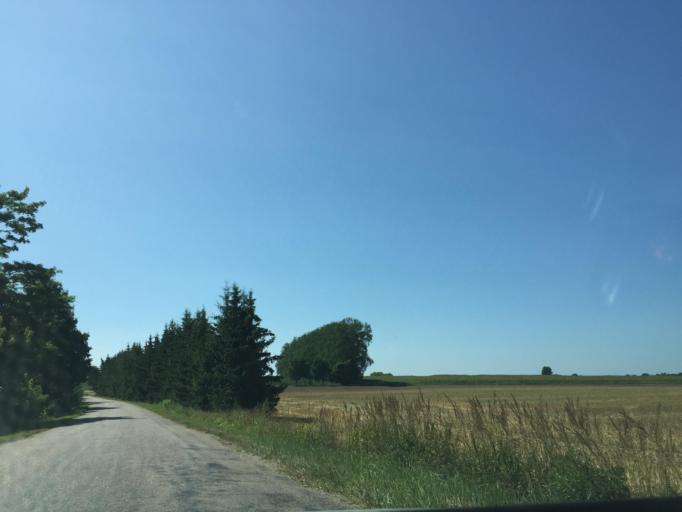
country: LV
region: Talsu Rajons
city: Talsi
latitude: 57.1455
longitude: 22.6664
